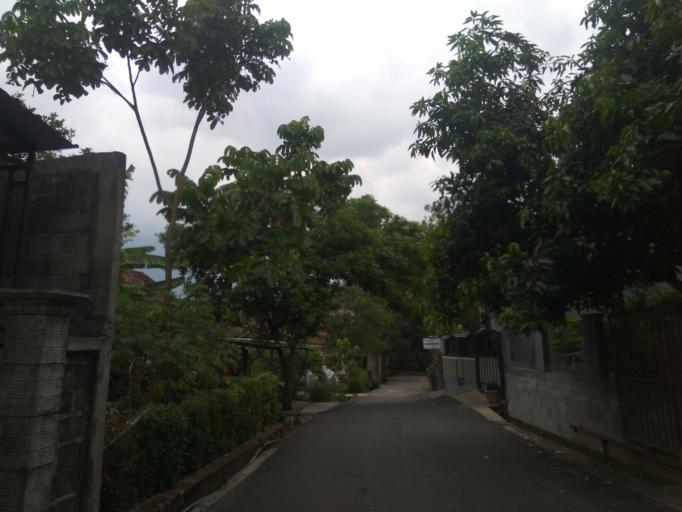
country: ID
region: Central Java
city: Semarang
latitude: -7.0634
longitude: 110.4404
